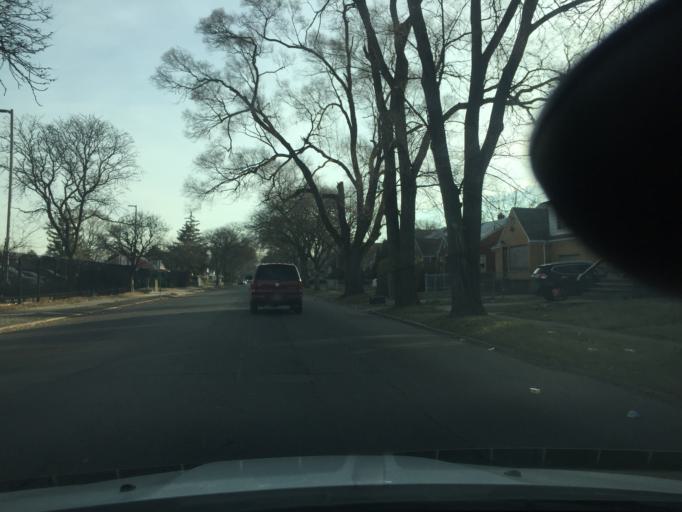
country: US
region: Michigan
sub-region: Macomb County
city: Eastpointe
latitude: 42.4425
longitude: -82.9718
